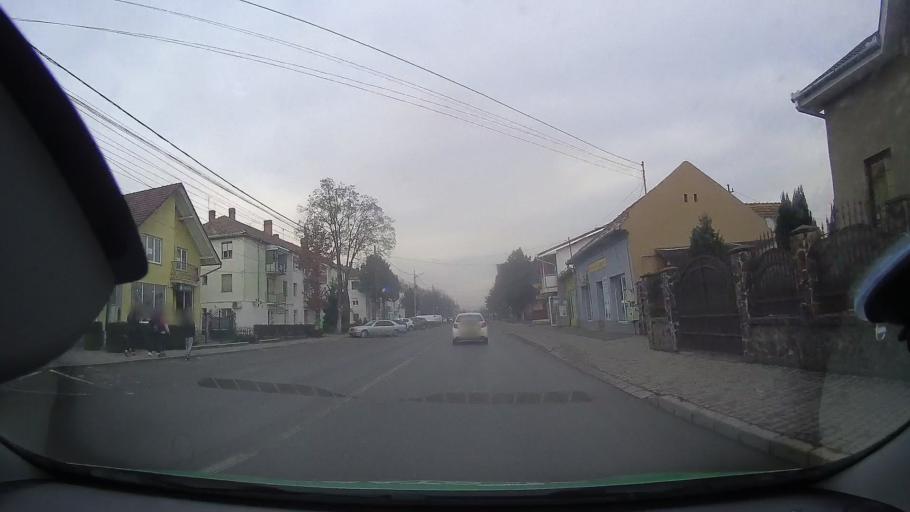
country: RO
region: Mures
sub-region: Comuna Ludus
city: Ludus
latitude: 46.4721
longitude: 24.0954
